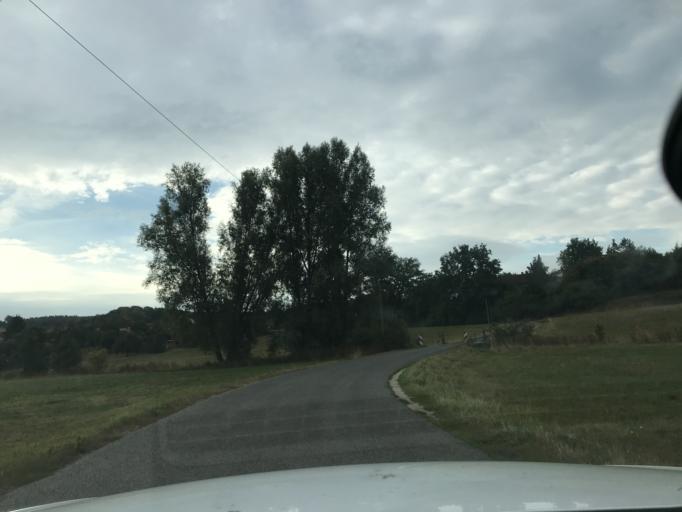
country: DE
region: Bavaria
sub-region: Upper Franconia
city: Pegnitz
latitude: 49.7475
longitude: 11.5554
